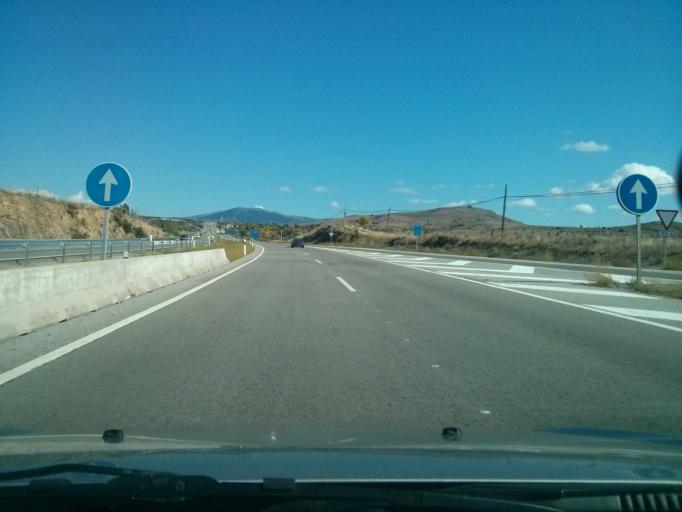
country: ES
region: Madrid
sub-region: Provincia de Madrid
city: Gascones
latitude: 41.0129
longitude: -3.6307
